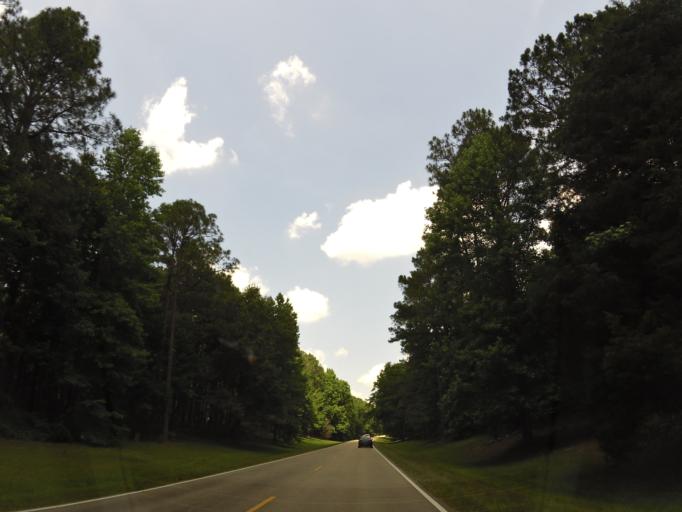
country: US
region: Mississippi
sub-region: Lee County
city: Tupelo
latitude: 34.3195
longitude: -88.7162
